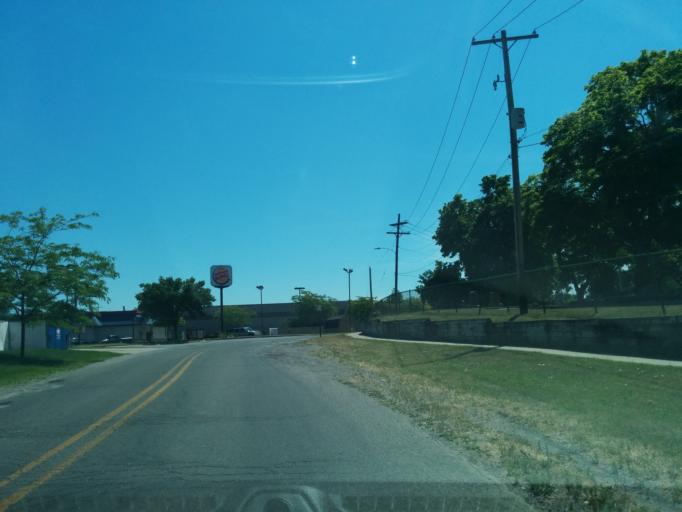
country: US
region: Michigan
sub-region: Bay County
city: Bay City
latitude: 43.6230
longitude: -83.8989
